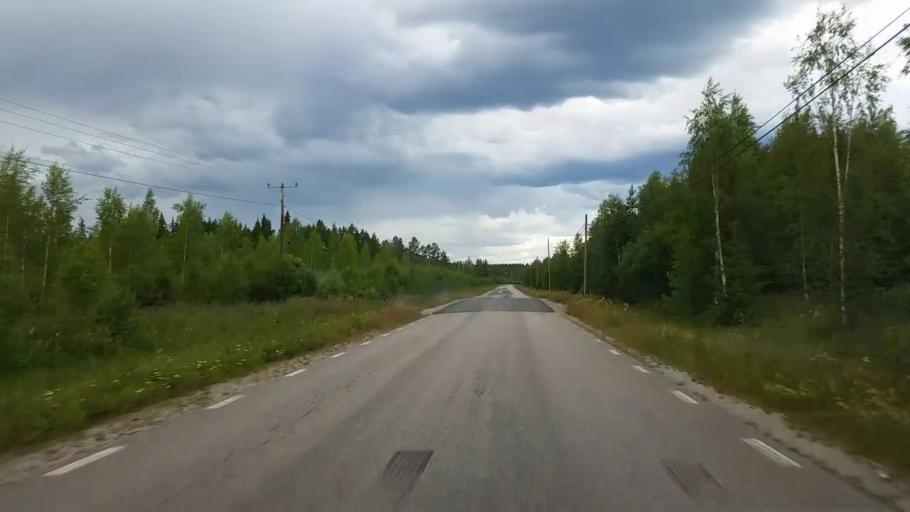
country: SE
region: Gaevleborg
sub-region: Ovanakers Kommun
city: Edsbyn
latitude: 61.4480
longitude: 15.8830
